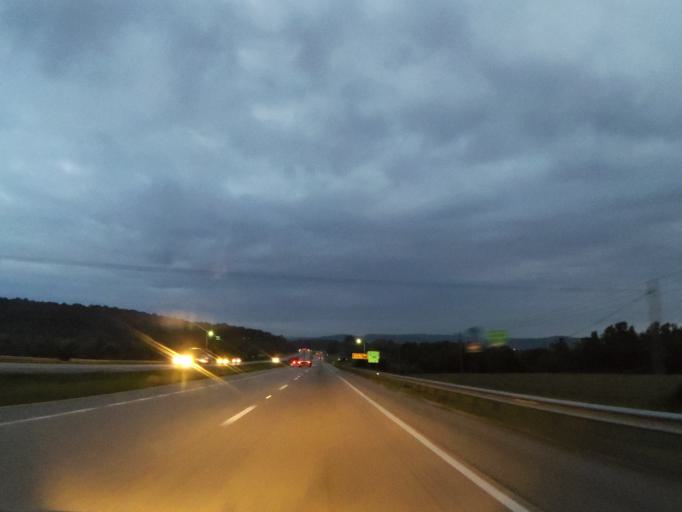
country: US
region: Alabama
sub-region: Madison County
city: New Hope
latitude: 34.6094
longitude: -86.2727
